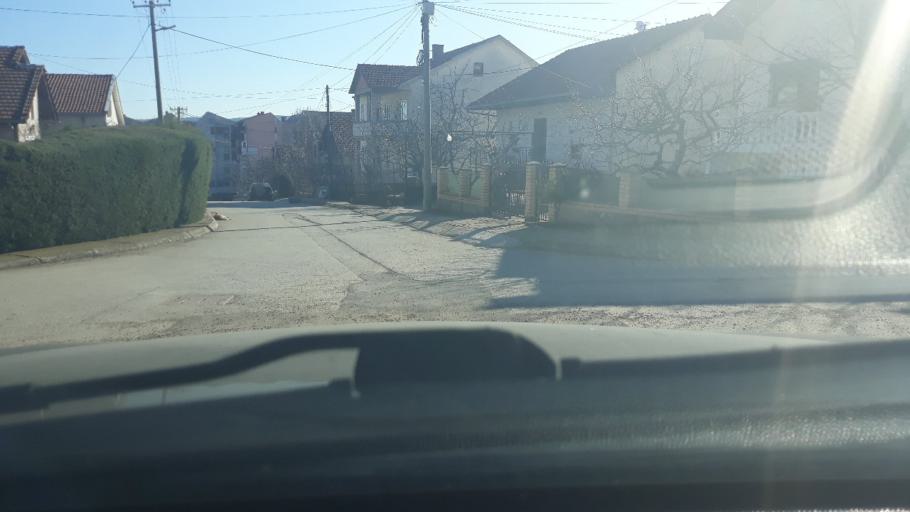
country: MK
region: Sveti Nikole
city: Sveti Nikole
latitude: 41.8685
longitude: 21.9306
